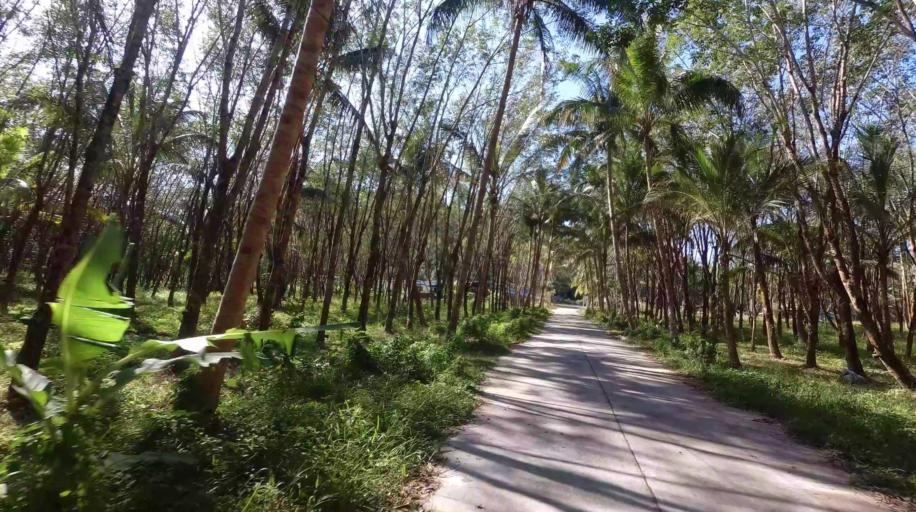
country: TH
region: Trat
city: Ko Kut
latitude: 11.6212
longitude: 102.5505
